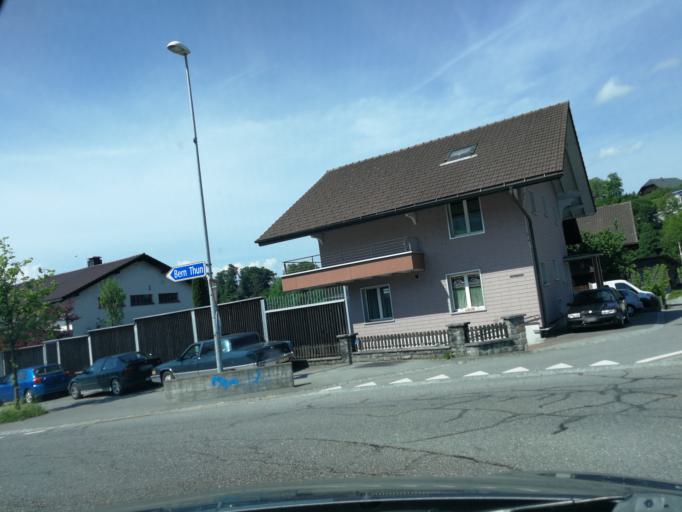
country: CH
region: Lucerne
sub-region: Entlebuch District
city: Oberdiessbach
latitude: 46.8370
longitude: 7.6182
